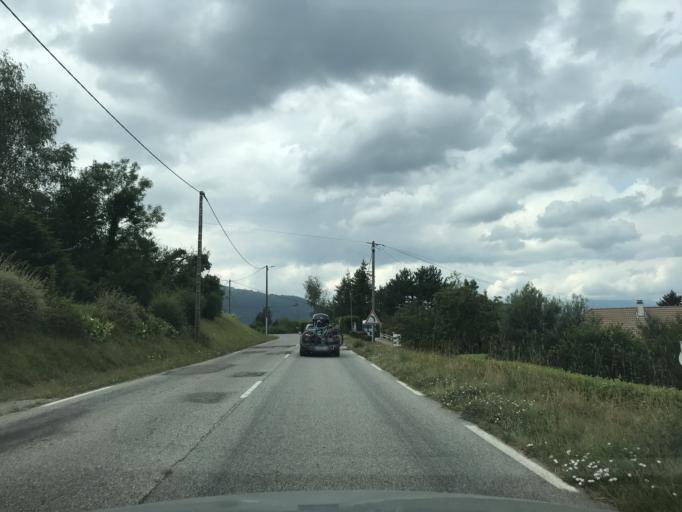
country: FR
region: Rhone-Alpes
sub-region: Departement de la Savoie
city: Brison-Saint-Innocent
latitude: 45.7332
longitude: 5.8858
